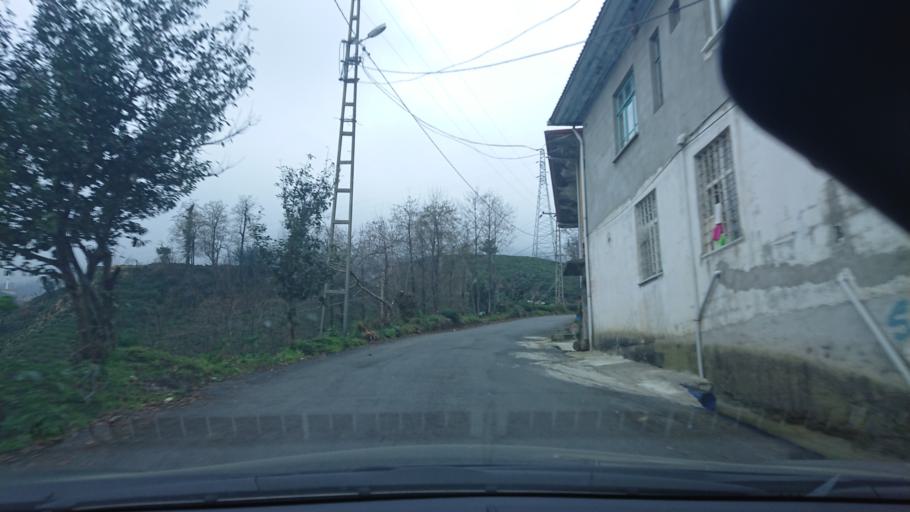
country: TR
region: Rize
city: Rize
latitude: 40.9955
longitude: 40.4910
